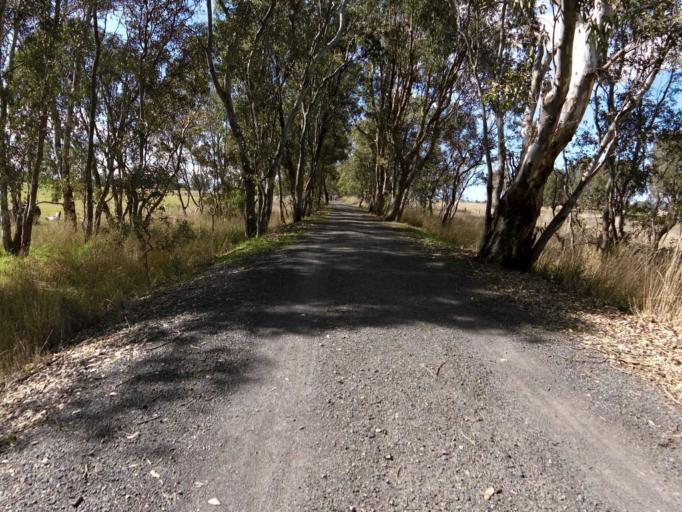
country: AU
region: Victoria
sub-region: Mansfield
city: Mansfield
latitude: -37.0483
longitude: 146.0634
